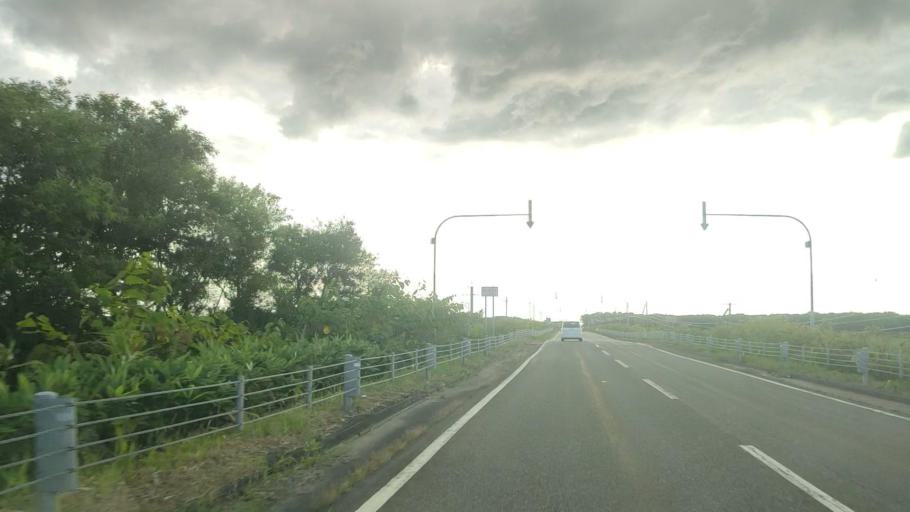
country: JP
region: Hokkaido
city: Makubetsu
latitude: 45.0045
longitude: 141.7998
